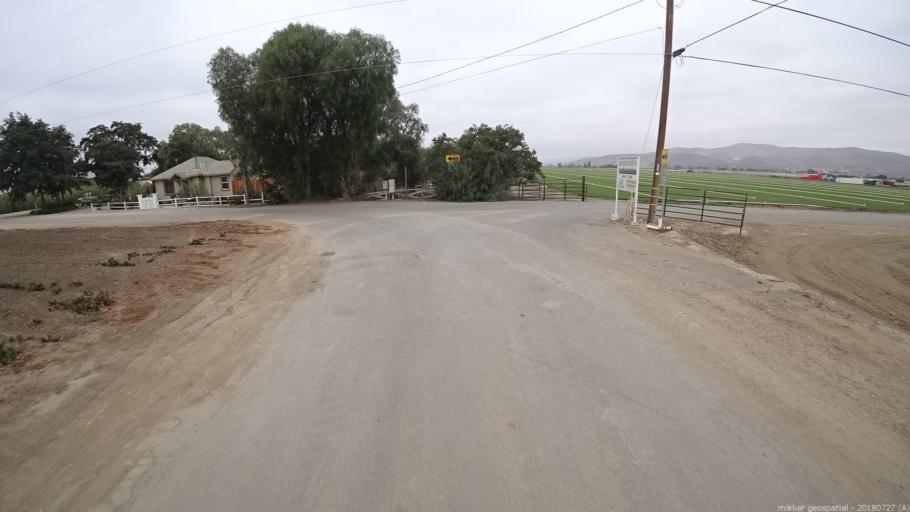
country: US
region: California
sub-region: Monterey County
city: Greenfield
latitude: 36.3352
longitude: -121.2175
